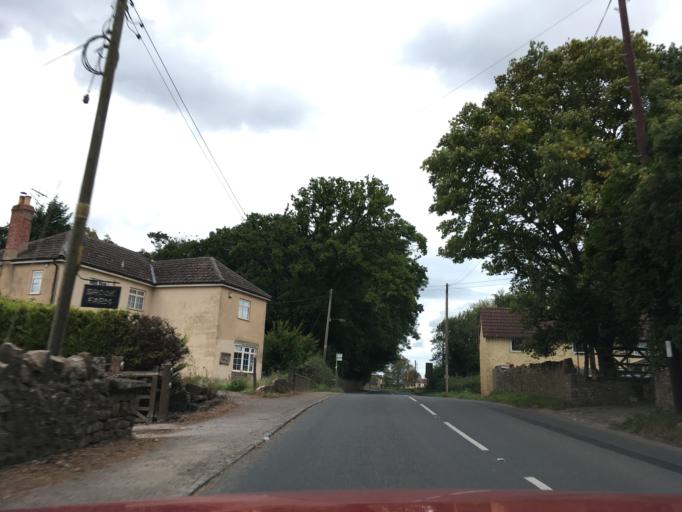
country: GB
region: England
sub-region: South Gloucestershire
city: Charfield
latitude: 51.6040
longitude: -2.4384
